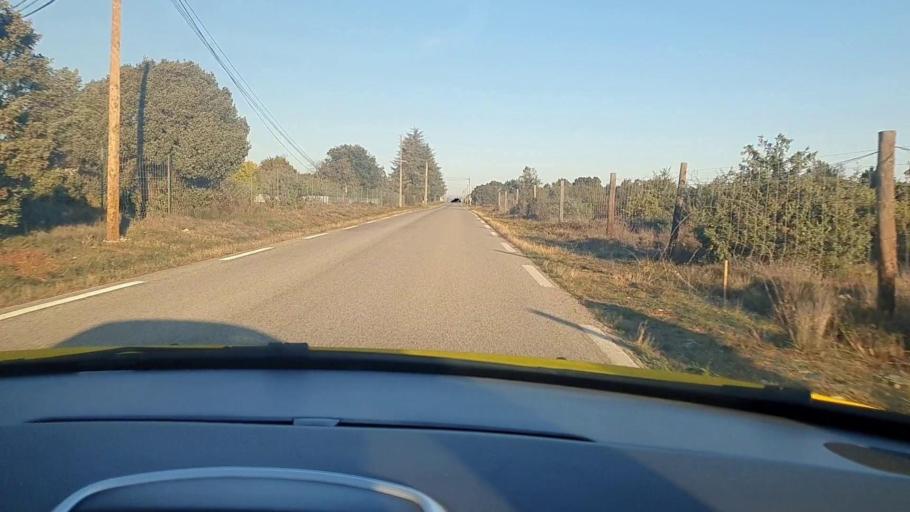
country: FR
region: Languedoc-Roussillon
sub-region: Departement du Gard
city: Montaren-et-Saint-Mediers
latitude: 44.1188
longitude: 4.3698
